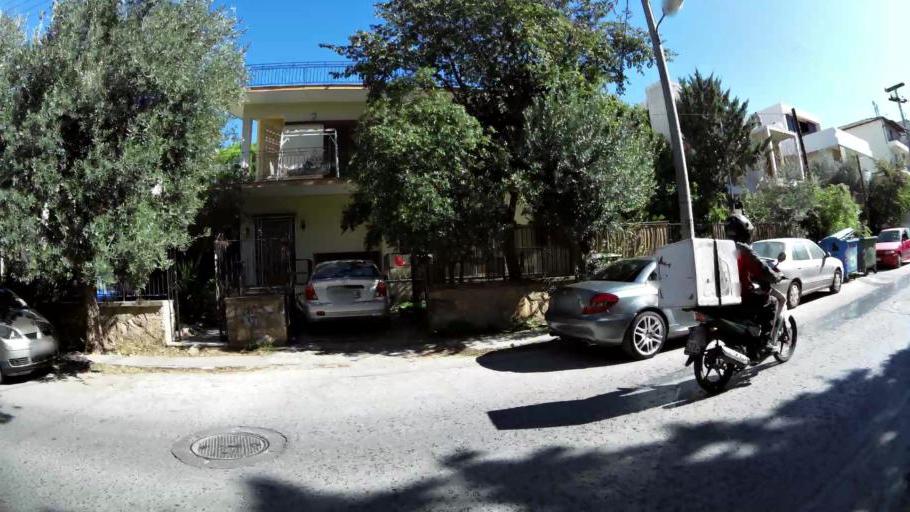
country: GR
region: Attica
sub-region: Nomarchia Athinas
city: Khalandrion
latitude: 38.0318
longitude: 23.8022
